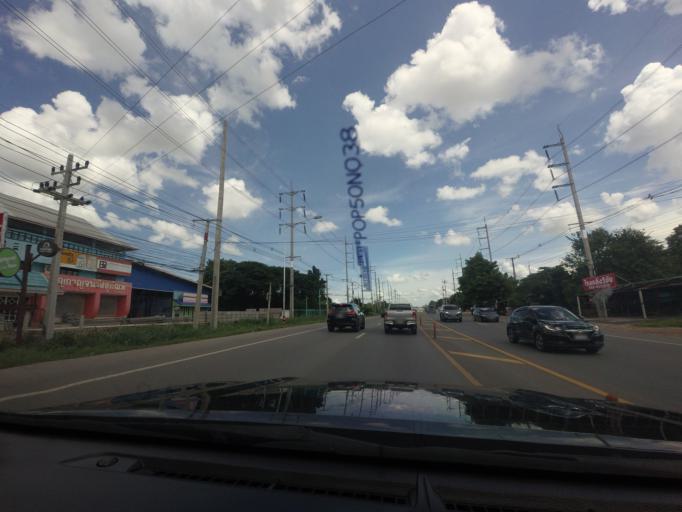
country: TH
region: Kanchanaburi
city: Kanchanaburi
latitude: 14.0708
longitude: 99.4864
